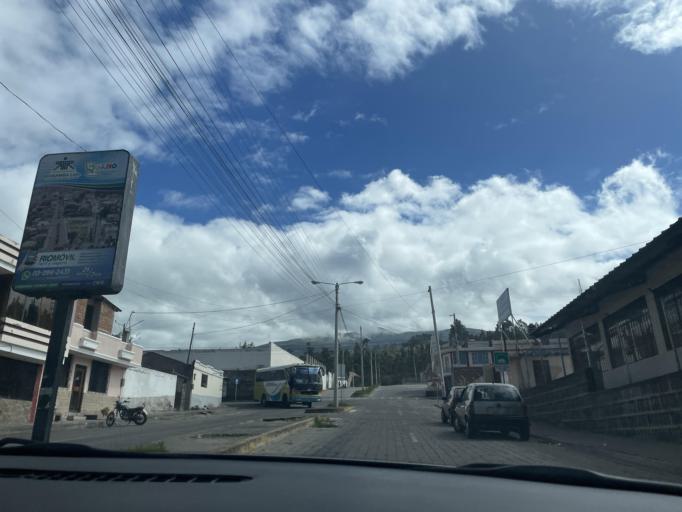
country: EC
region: Chimborazo
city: Guano
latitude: -1.6032
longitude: -78.6426
